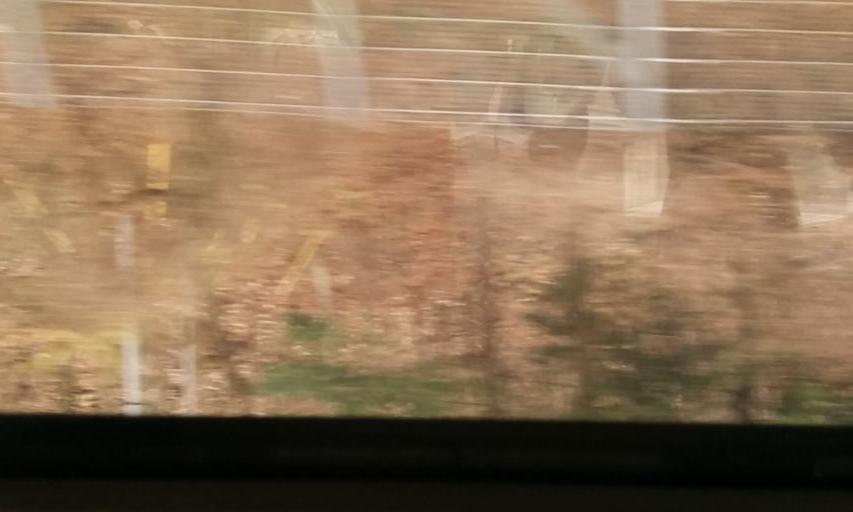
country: JP
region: Nagano
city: Ina
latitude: 35.8260
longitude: 137.6823
